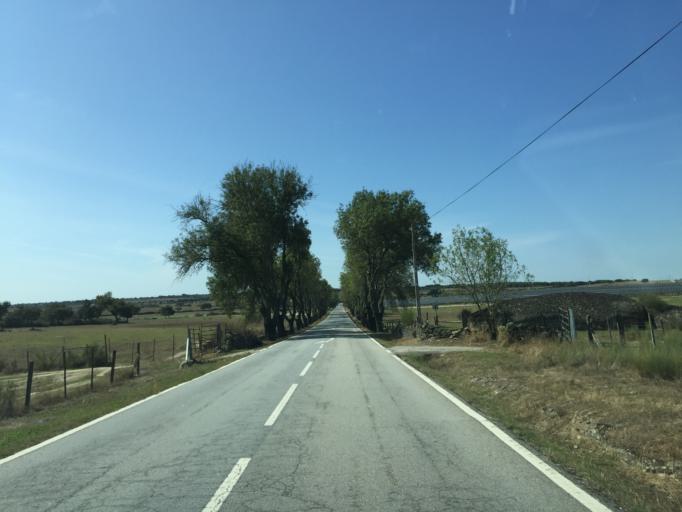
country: PT
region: Portalegre
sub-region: Portalegre
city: Alagoa
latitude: 39.4317
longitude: -7.5806
